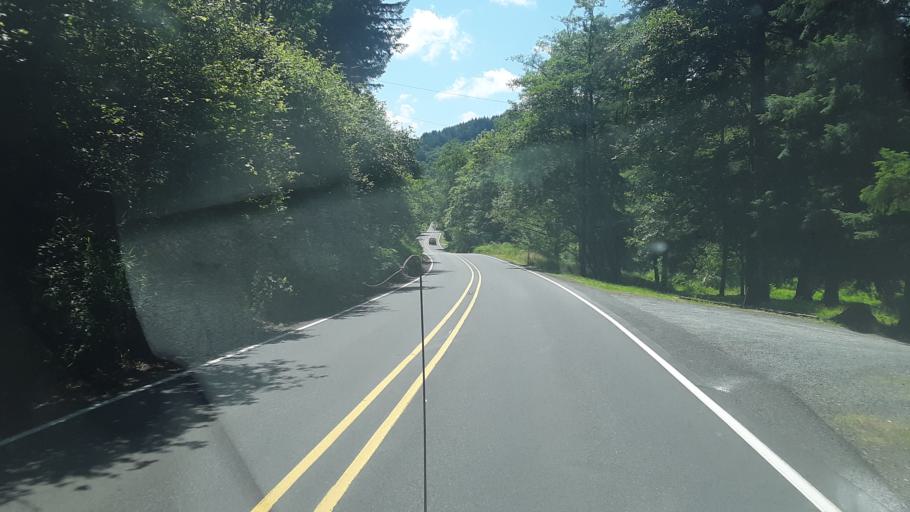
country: US
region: Washington
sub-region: Clark County
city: Amboy
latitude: 45.9334
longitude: -122.3798
